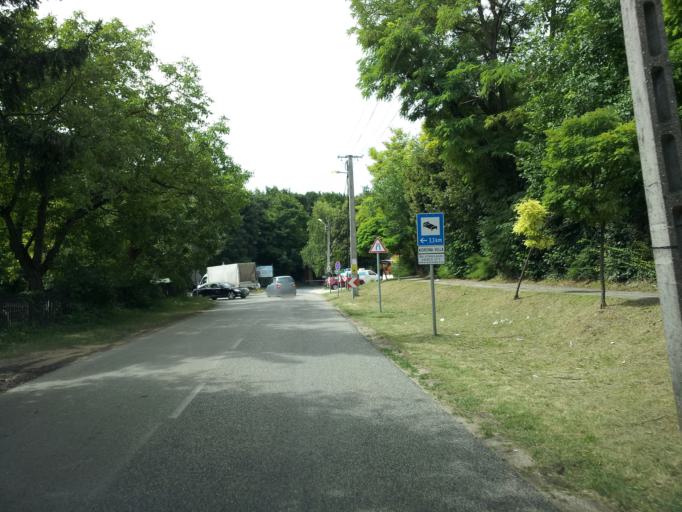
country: HU
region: Fejer
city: Lepseny
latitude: 46.9860
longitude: 18.1725
